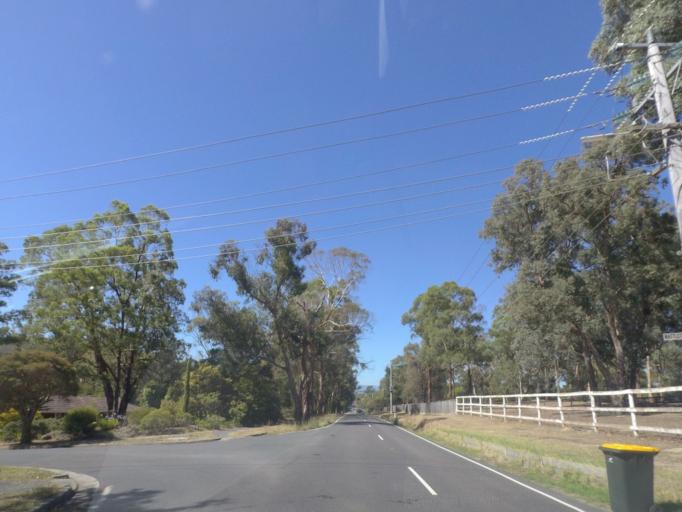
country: AU
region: Victoria
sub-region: Yarra Ranges
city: Chirnside Park
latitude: -37.7423
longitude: 145.2780
